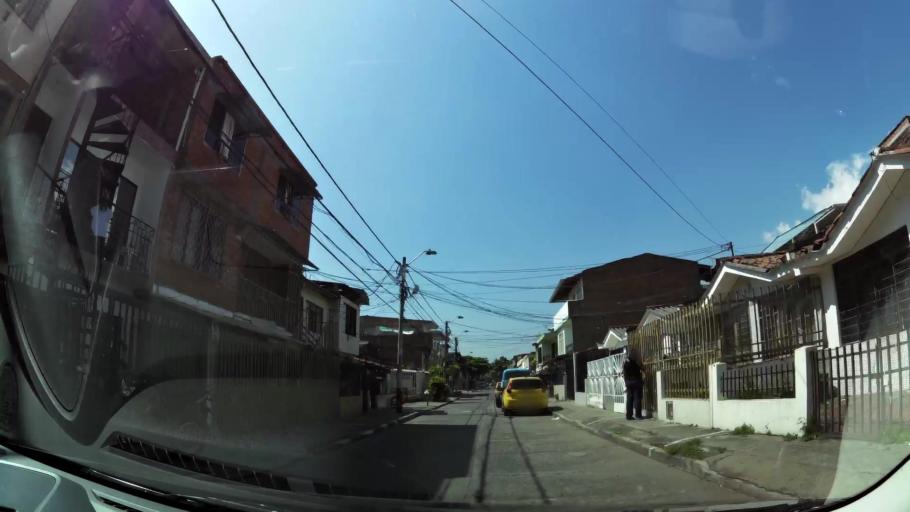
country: CO
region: Valle del Cauca
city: Cali
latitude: 3.4098
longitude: -76.5250
